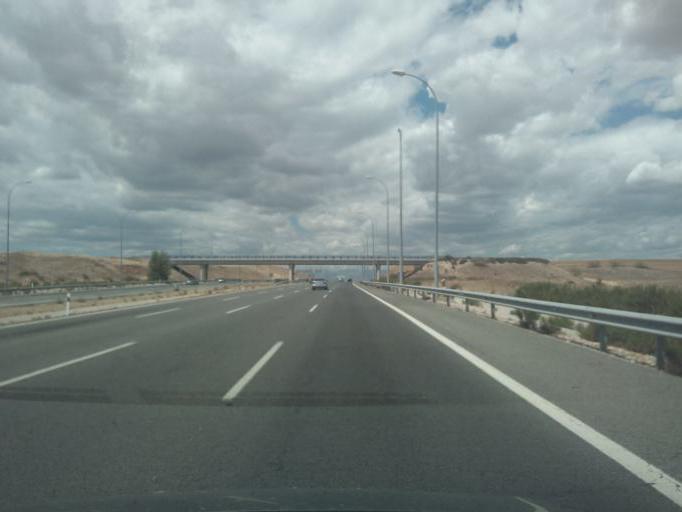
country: ES
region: Madrid
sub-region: Provincia de Madrid
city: Paracuellos de Jarama
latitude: 40.5244
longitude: -3.5104
